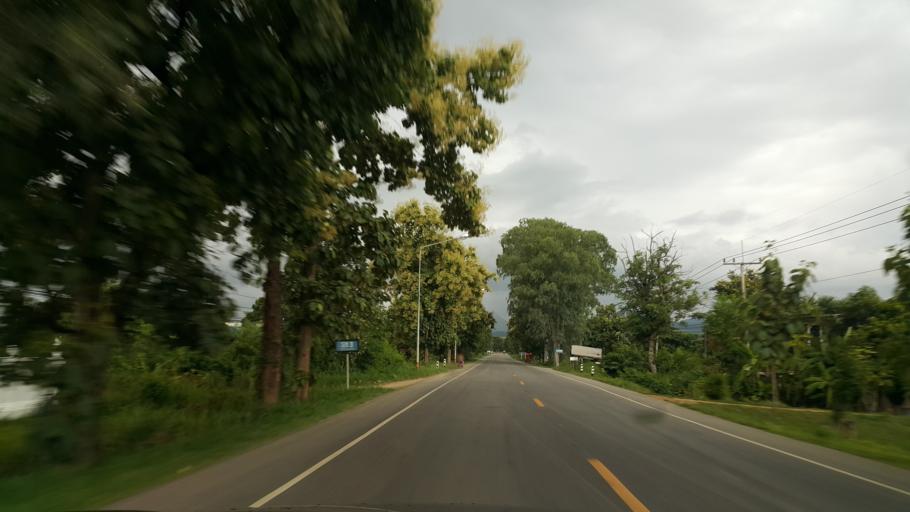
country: TH
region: Phayao
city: Dok Kham Tai
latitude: 19.2248
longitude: 100.0454
